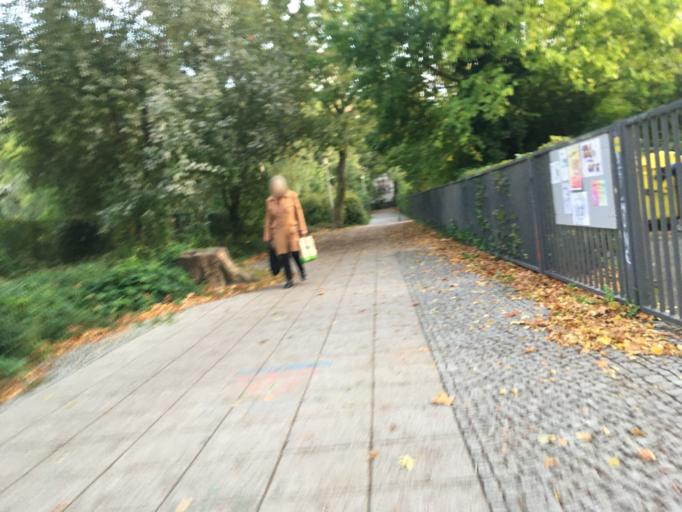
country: DE
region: Berlin
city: Pankow
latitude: 52.5715
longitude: 13.4049
